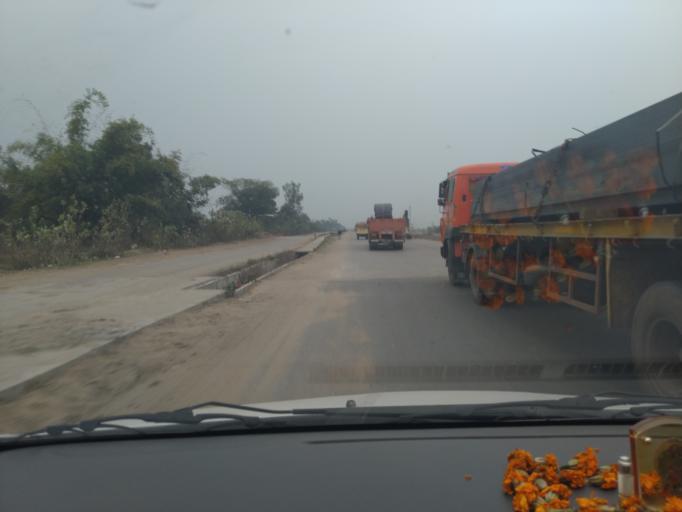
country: IN
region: Bihar
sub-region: Rohtas
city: Dehri
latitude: 24.9714
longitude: 83.9146
